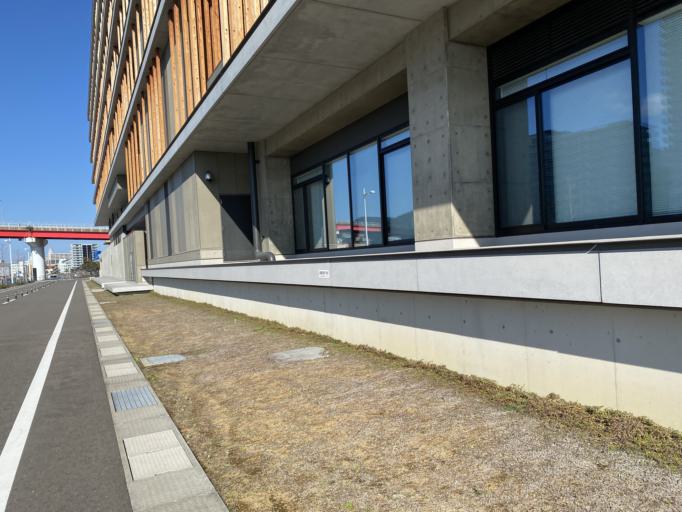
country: JP
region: Nagasaki
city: Nagasaki-shi
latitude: 32.7497
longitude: 129.8670
